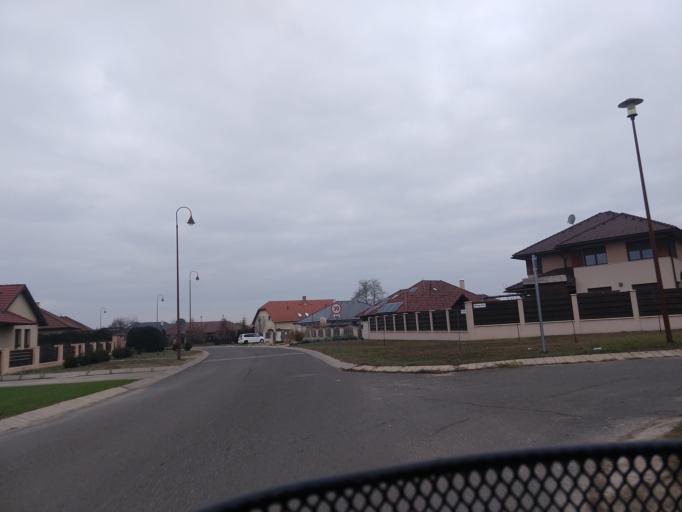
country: HU
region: Pest
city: Orbottyan
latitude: 47.6597
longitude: 19.2559
